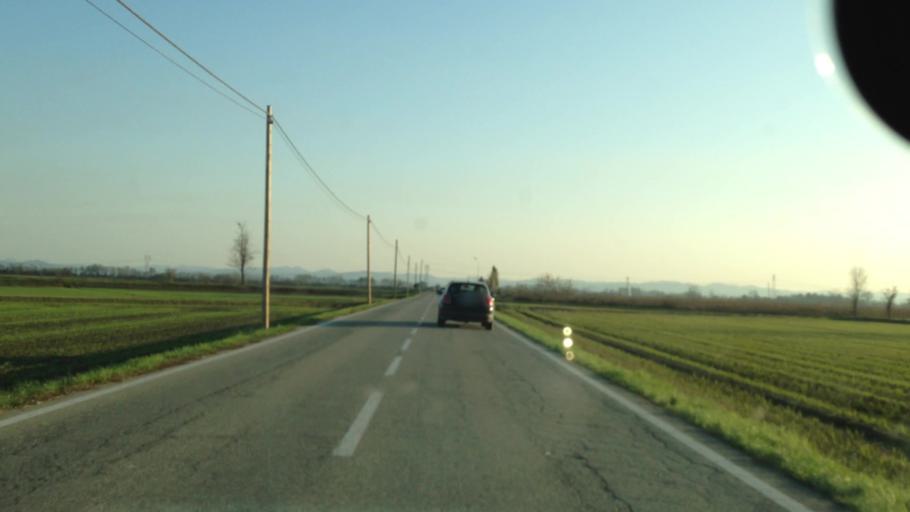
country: IT
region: Piedmont
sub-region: Provincia di Vercelli
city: Lamporo
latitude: 45.2553
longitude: 8.0864
